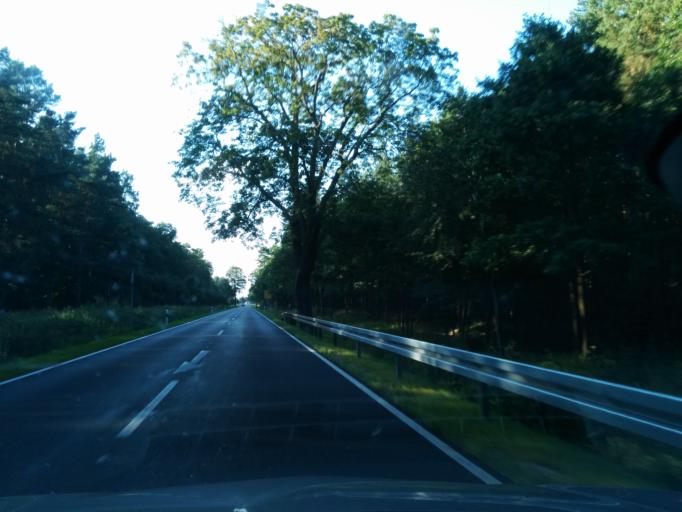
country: DE
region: Mecklenburg-Vorpommern
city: Ferdinandshof
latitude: 53.6374
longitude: 13.9197
